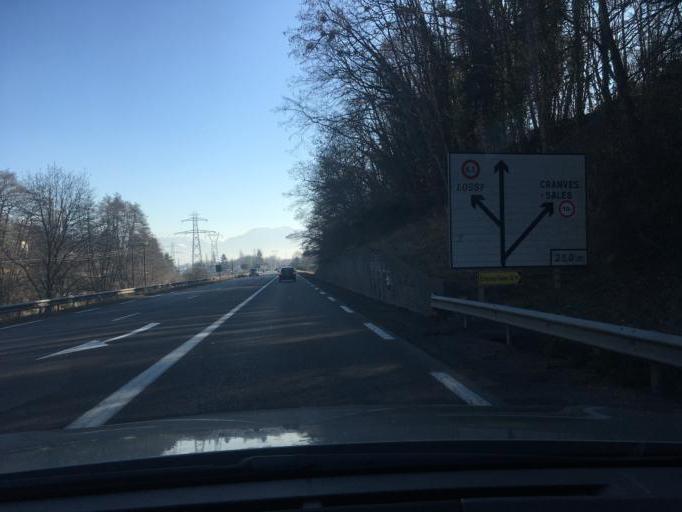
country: FR
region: Rhone-Alpes
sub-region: Departement de la Haute-Savoie
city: Cranves-Sales
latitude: 46.1944
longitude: 6.2922
